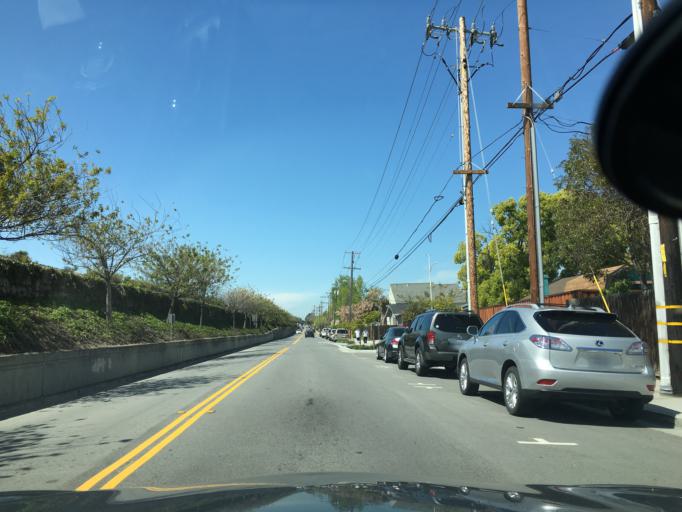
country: US
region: California
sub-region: San Mateo County
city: San Carlos
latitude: 37.5114
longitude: -122.2639
